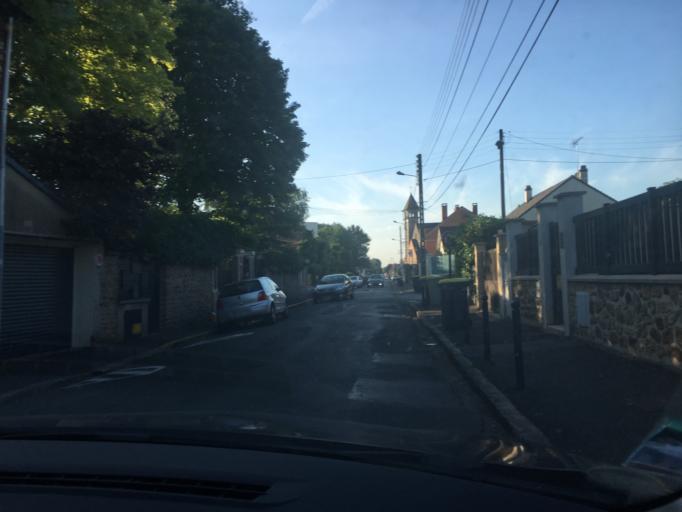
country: FR
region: Ile-de-France
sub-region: Departement de l'Essonne
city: Brunoy
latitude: 48.6939
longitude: 2.4906
